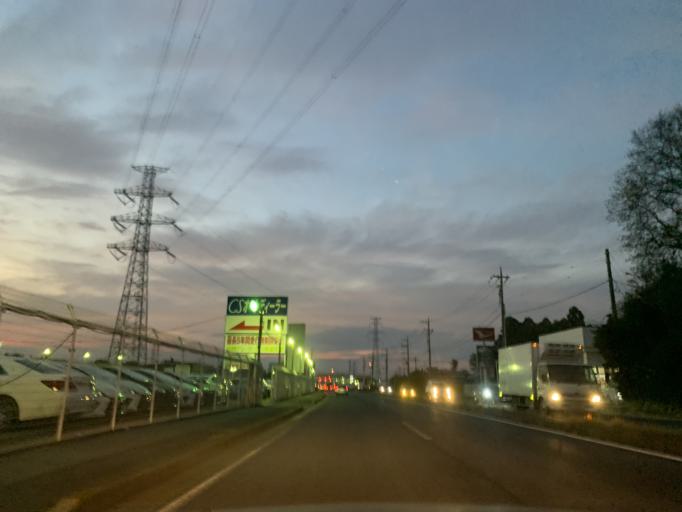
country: JP
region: Chiba
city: Nagareyama
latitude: 35.9208
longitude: 139.9228
